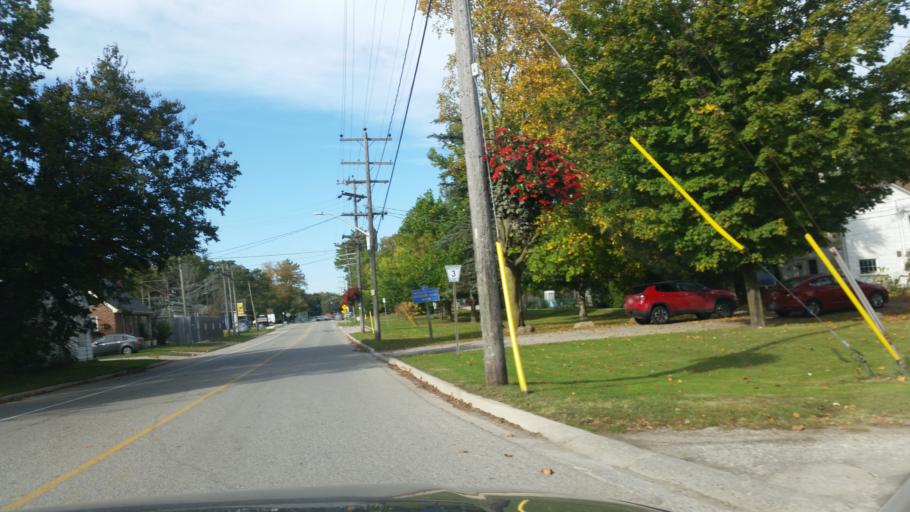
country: CA
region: Ontario
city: Delaware
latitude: 42.9078
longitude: -81.4213
